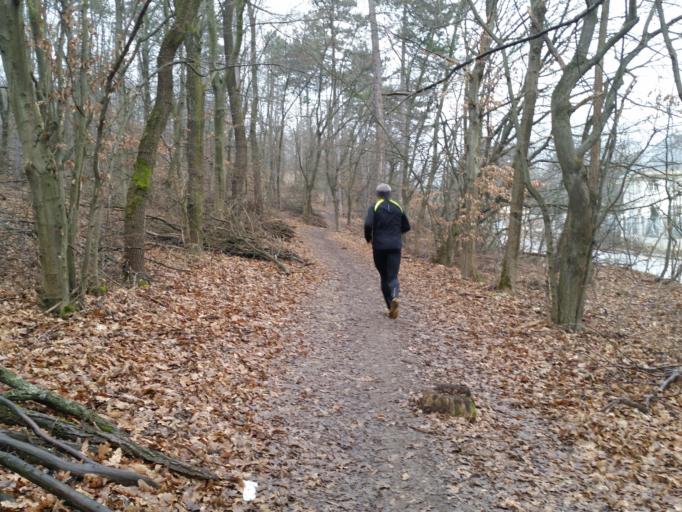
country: HU
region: Budapest
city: Budapest II. keruelet
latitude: 47.5424
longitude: 18.9978
